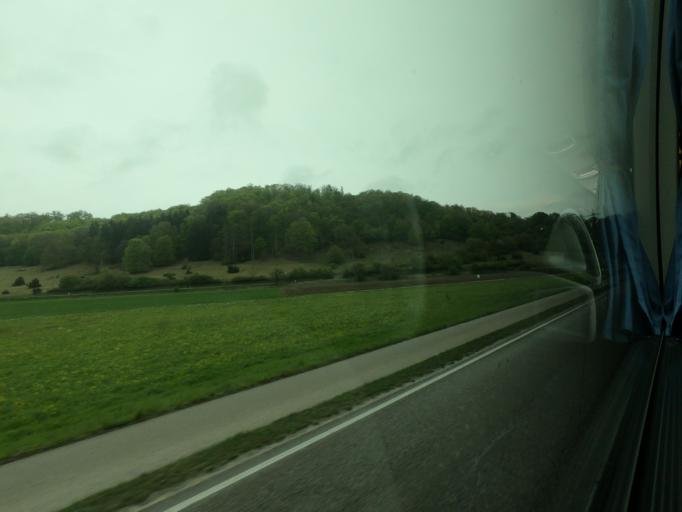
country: DE
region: Baden-Wuerttemberg
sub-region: Regierungsbezirk Stuttgart
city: Konigsbronn
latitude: 48.7290
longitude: 10.1554
